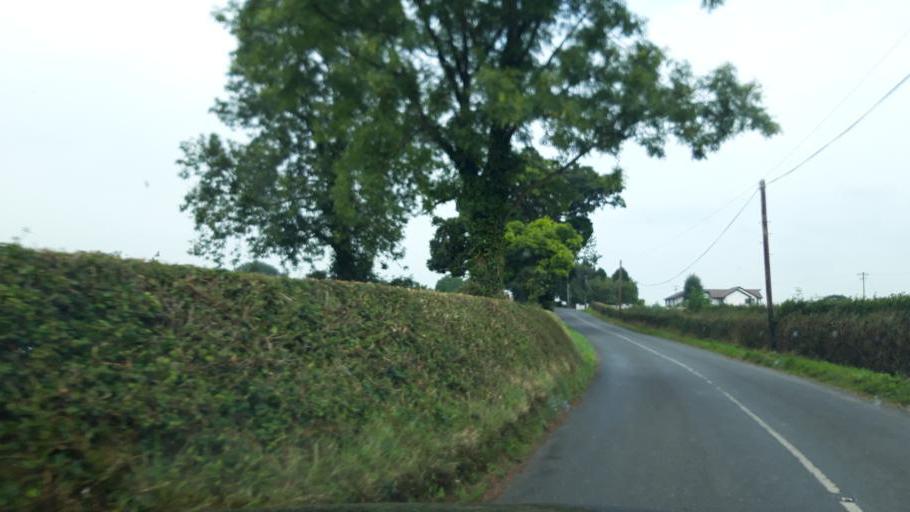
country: IE
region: Leinster
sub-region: Kilkenny
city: Callan
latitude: 52.5108
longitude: -7.4815
